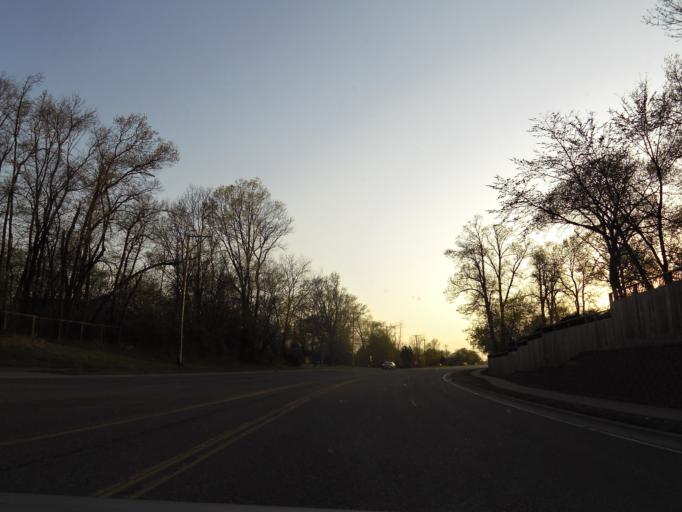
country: US
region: Minnesota
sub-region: Scott County
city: Savage
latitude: 44.7649
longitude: -93.3519
